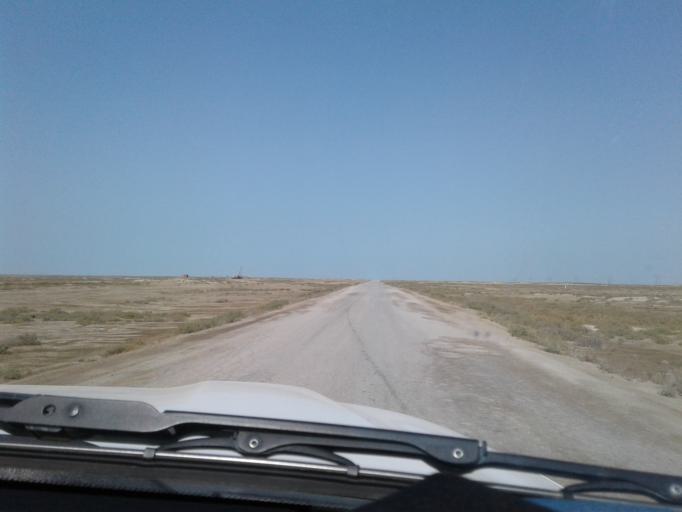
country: IR
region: Golestan
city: Gomishan
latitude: 37.8350
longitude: 53.9091
